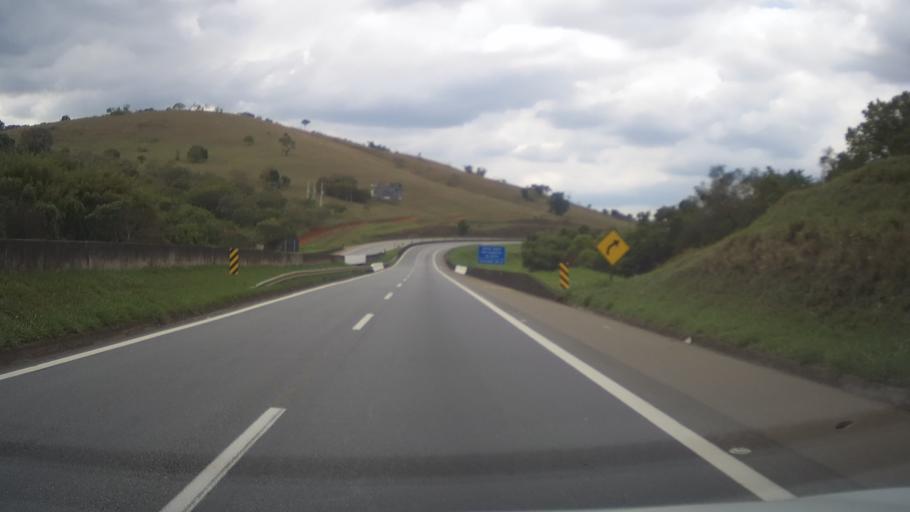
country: BR
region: Minas Gerais
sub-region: Tres Coracoes
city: Tres Coracoes
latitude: -21.5214
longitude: -45.2234
